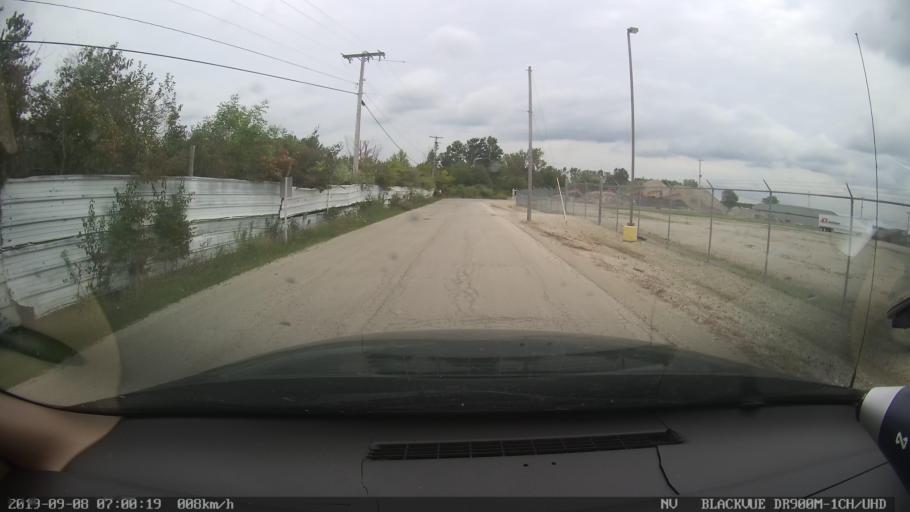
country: US
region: Ohio
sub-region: Richland County
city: Shelby
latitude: 40.8994
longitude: -82.6761
